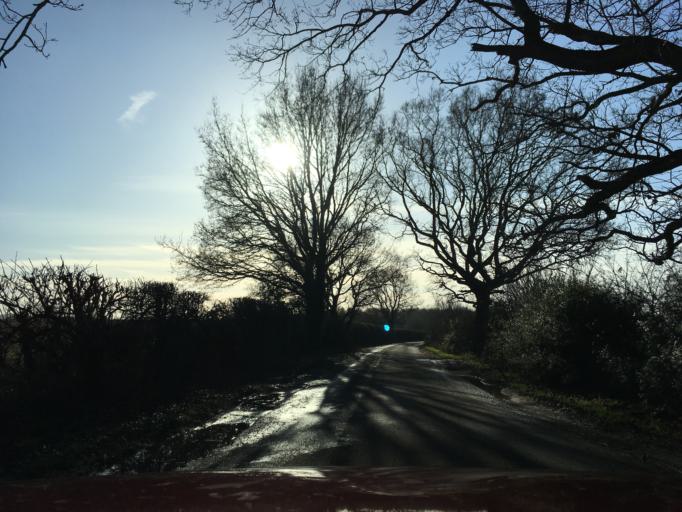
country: GB
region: England
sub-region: Warwickshire
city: Stratford-upon-Avon
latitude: 52.1976
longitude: -1.6629
